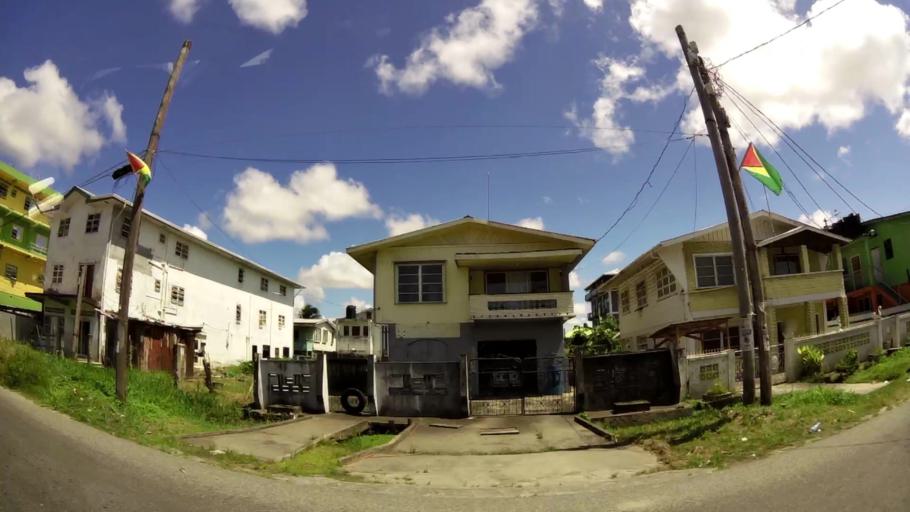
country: GY
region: Demerara-Mahaica
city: Georgetown
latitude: 6.8023
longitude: -58.1505
